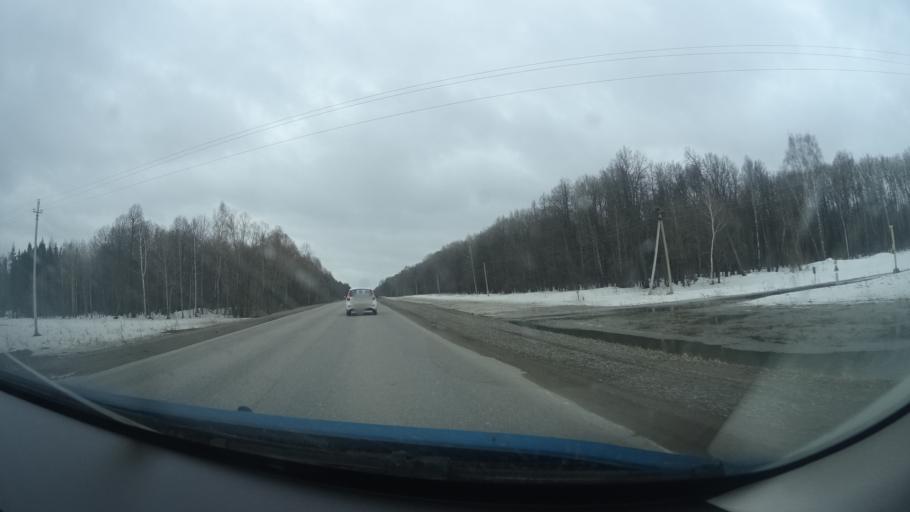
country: RU
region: Bashkortostan
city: Birsk
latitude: 55.3256
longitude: 55.6097
